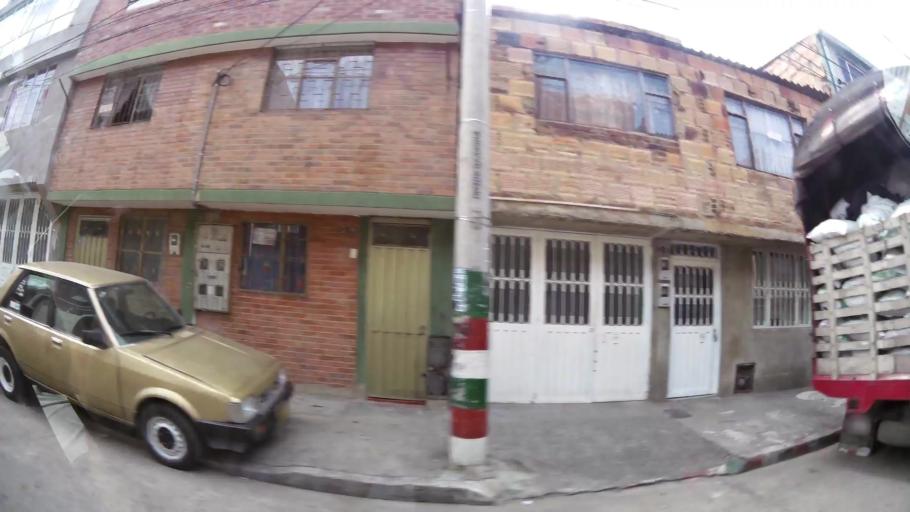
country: CO
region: Bogota D.C.
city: Bogota
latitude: 4.6226
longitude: -74.1275
